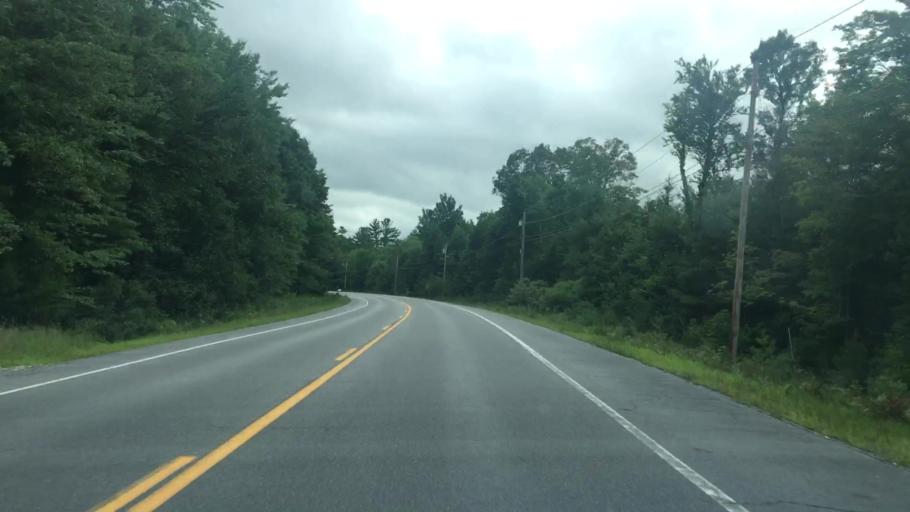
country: US
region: Maine
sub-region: York County
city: Limerick
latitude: 43.7388
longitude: -70.8162
